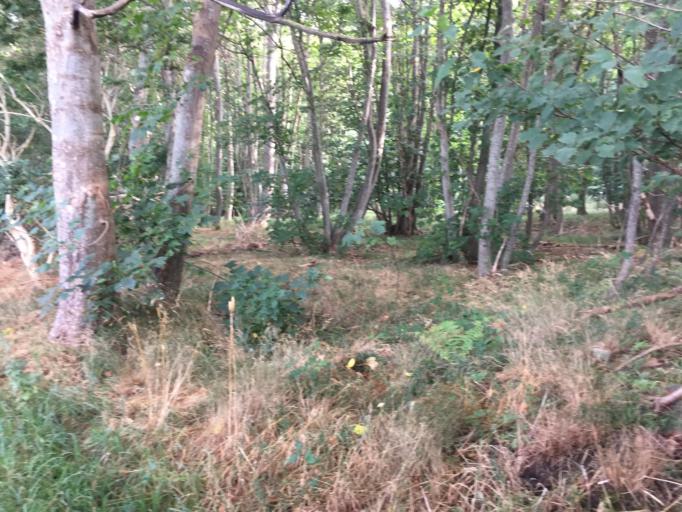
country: DK
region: South Denmark
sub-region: Assens Kommune
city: Harby
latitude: 55.1405
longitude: 10.0300
